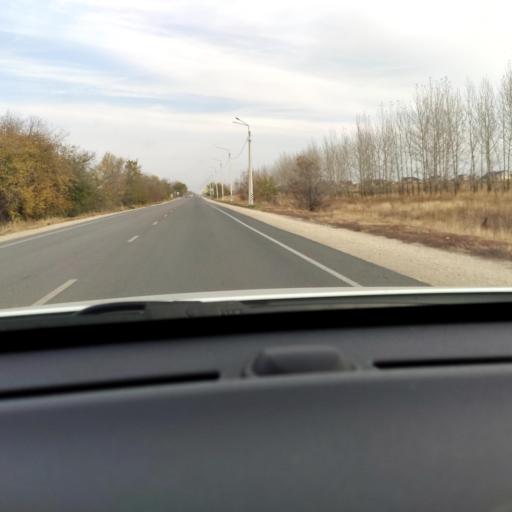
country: RU
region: Voronezj
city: Novaya Usman'
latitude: 51.6605
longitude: 39.4412
